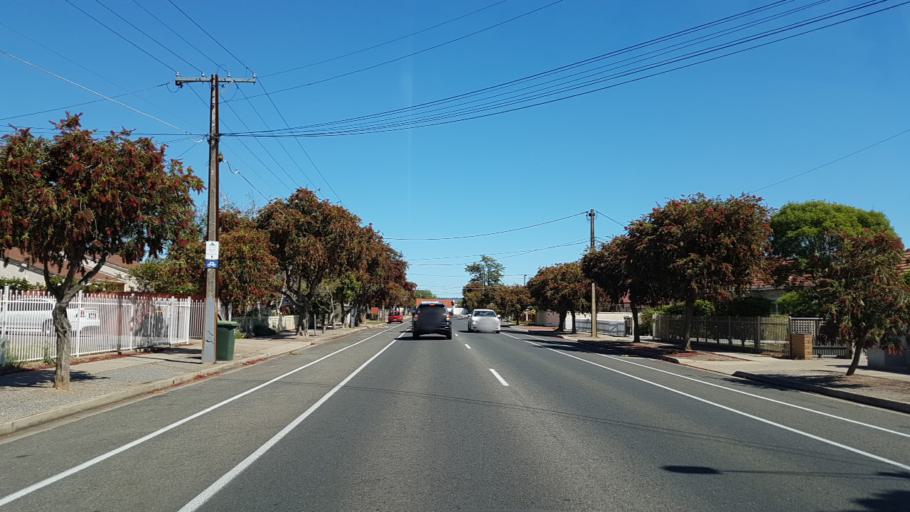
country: AU
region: South Australia
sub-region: Marion
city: South Plympton
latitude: -34.9658
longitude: 138.5637
